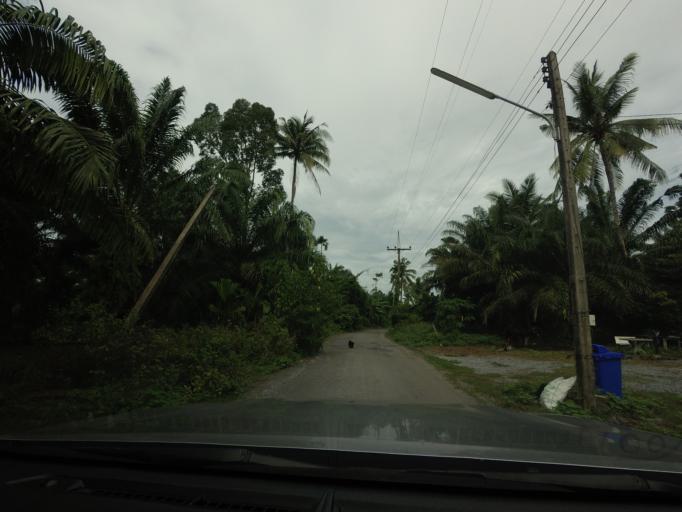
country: TH
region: Nakhon Si Thammarat
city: Phra Phrom
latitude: 8.2831
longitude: 99.9246
